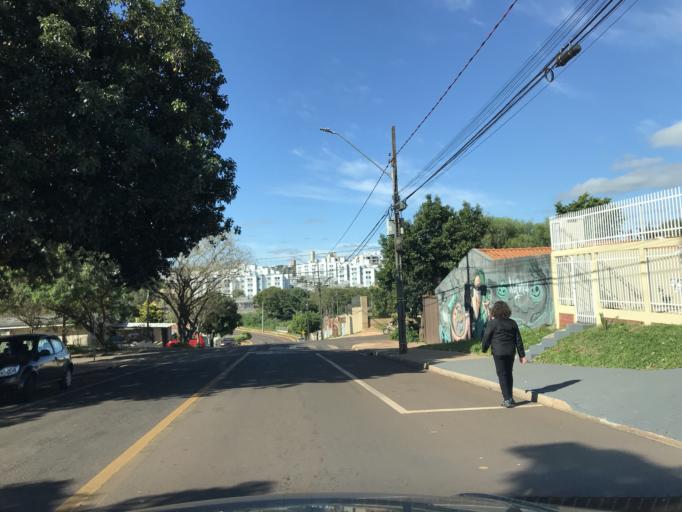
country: BR
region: Parana
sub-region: Cascavel
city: Cascavel
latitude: -24.9360
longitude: -53.4745
